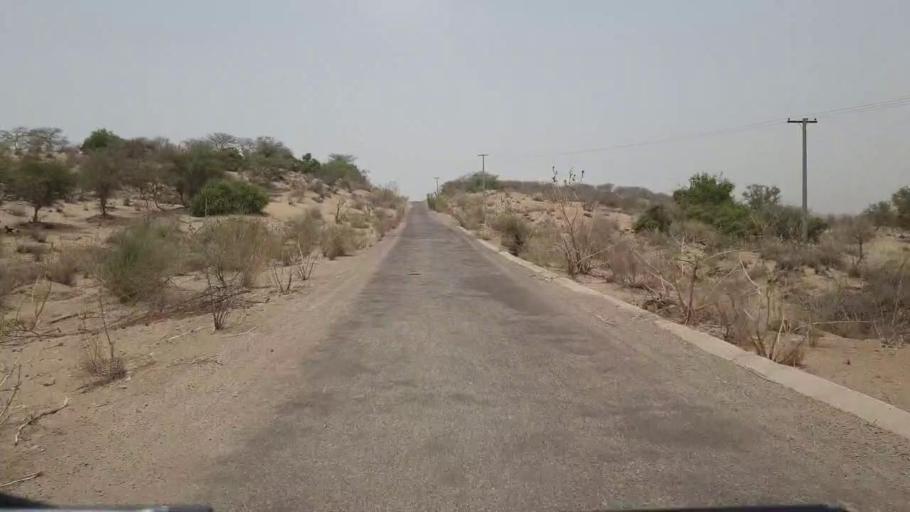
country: PK
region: Sindh
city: Naukot
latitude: 24.7458
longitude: 69.5495
